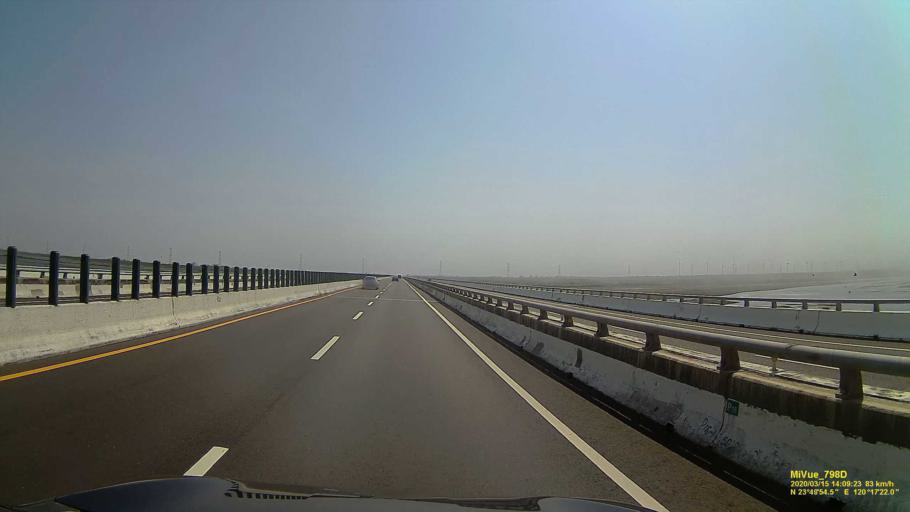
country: TW
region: Taiwan
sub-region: Yunlin
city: Douliu
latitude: 23.8320
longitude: 120.2895
